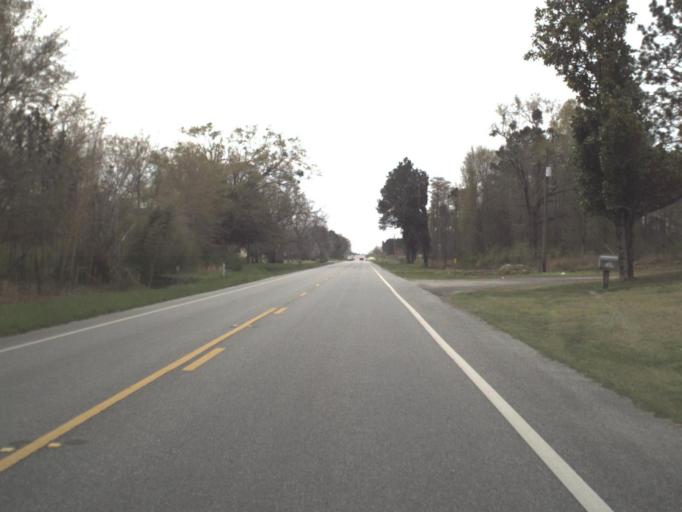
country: US
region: Florida
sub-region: Jackson County
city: Graceville
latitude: 30.9329
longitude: -85.6491
